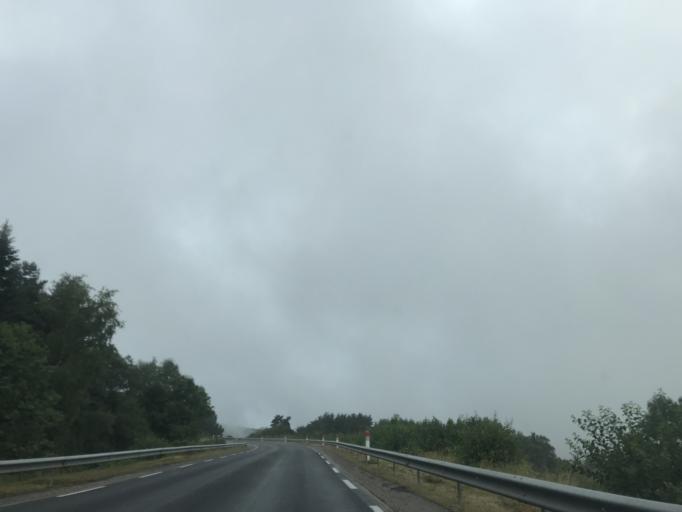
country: FR
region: Auvergne
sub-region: Departement de la Haute-Loire
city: Fontannes
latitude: 45.3487
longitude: 3.7316
